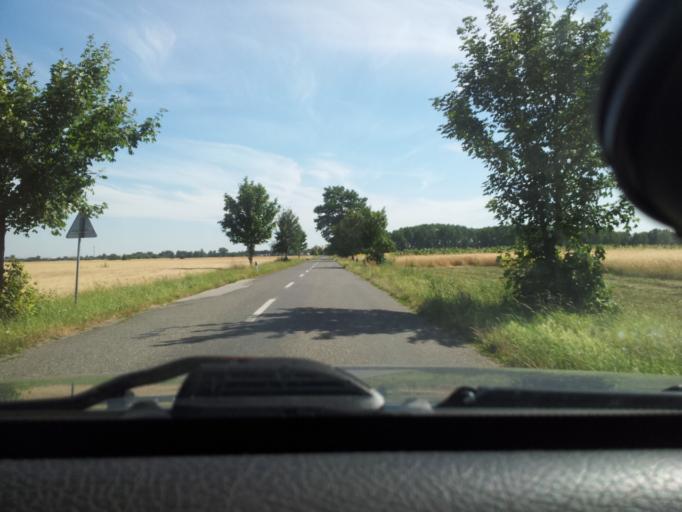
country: SK
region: Nitriansky
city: Tlmace
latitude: 48.2633
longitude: 18.5358
